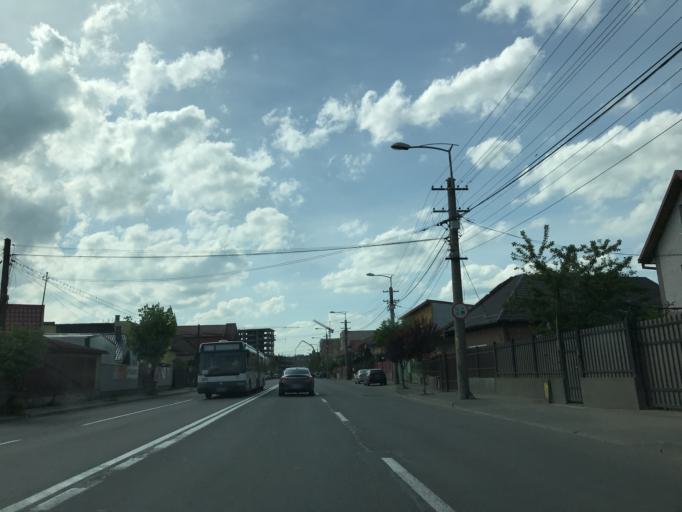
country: RO
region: Cluj
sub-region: Municipiul Cluj-Napoca
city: Cluj-Napoca
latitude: 46.7883
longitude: 23.6196
